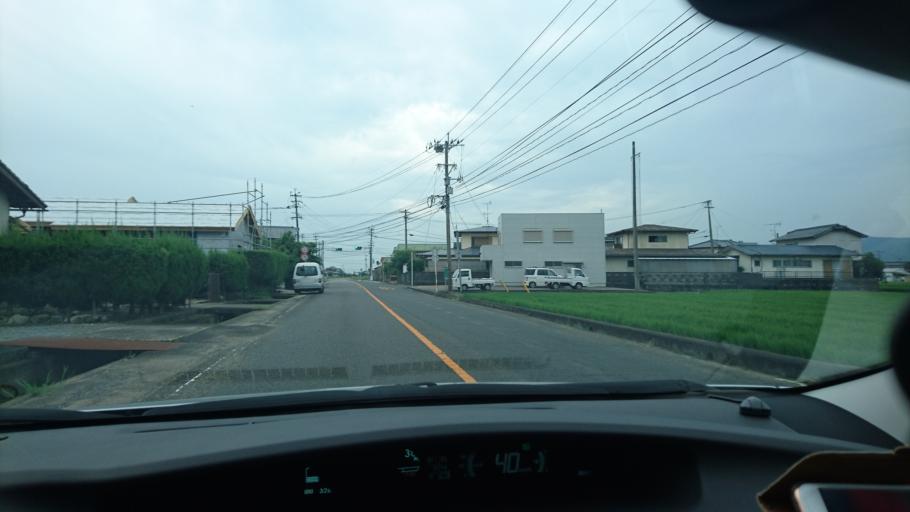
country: JP
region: Saga Prefecture
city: Takeocho-takeo
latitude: 33.2092
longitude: 130.1214
